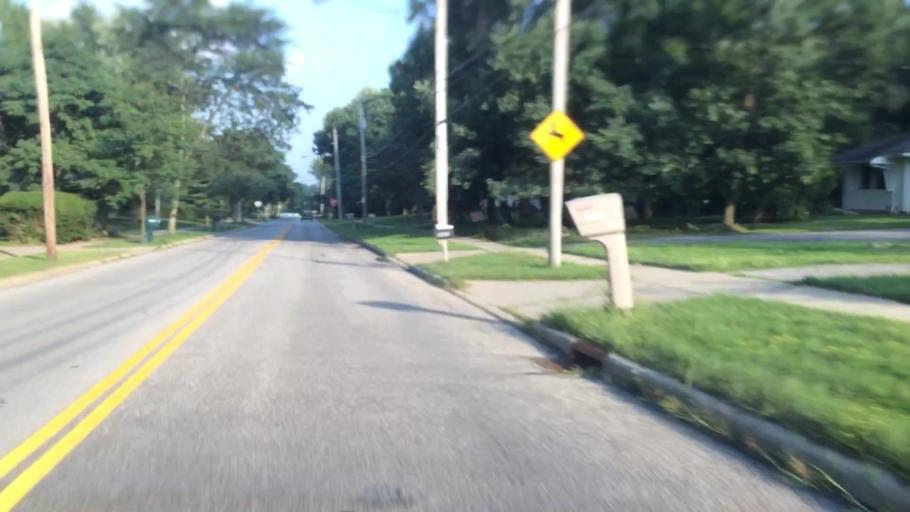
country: US
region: Ohio
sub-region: Cuyahoga County
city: Brecksville
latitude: 41.3315
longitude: -81.6426
